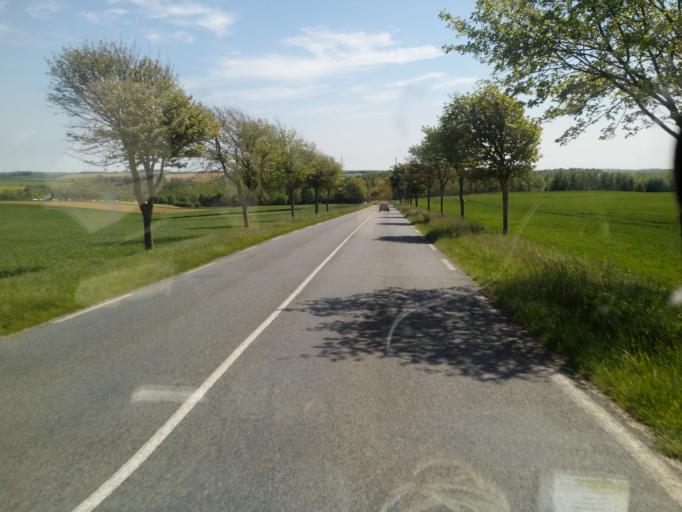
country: FR
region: Nord-Pas-de-Calais
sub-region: Departement du Pas-de-Calais
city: Samer
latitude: 50.5820
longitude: 1.7404
